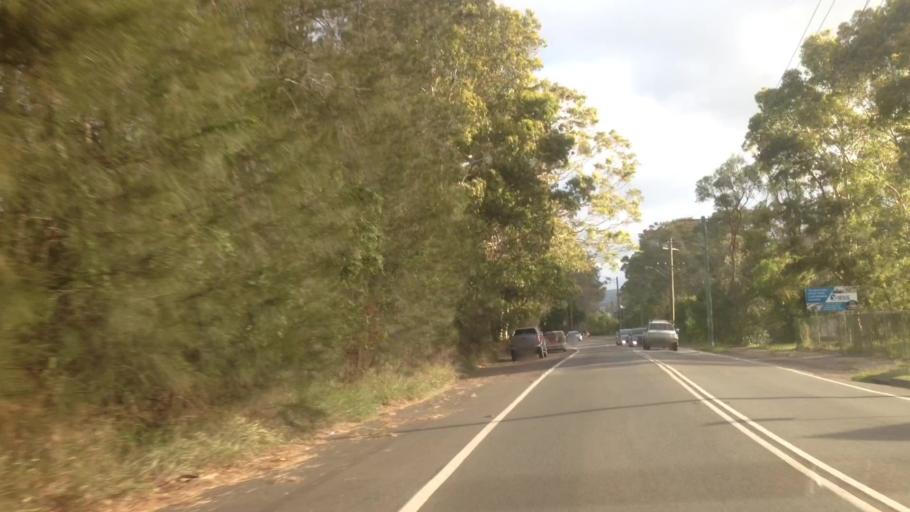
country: AU
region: New South Wales
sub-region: Wyong Shire
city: Chittaway Bay
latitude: -33.2875
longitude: 151.4244
